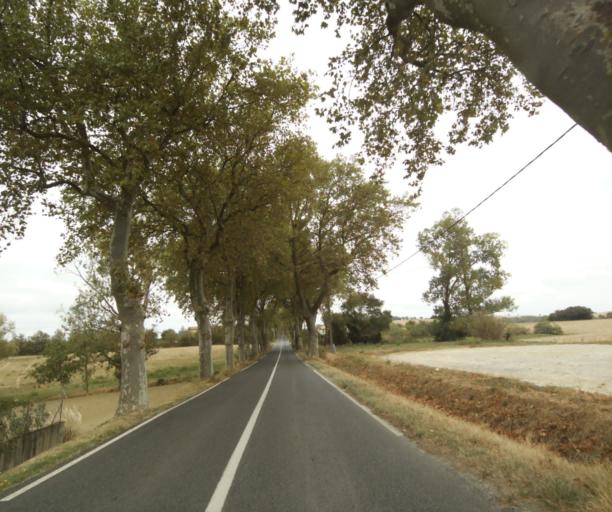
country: FR
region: Midi-Pyrenees
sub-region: Departement de la Haute-Garonne
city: Villefranche-de-Lauragais
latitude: 43.4044
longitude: 1.7256
